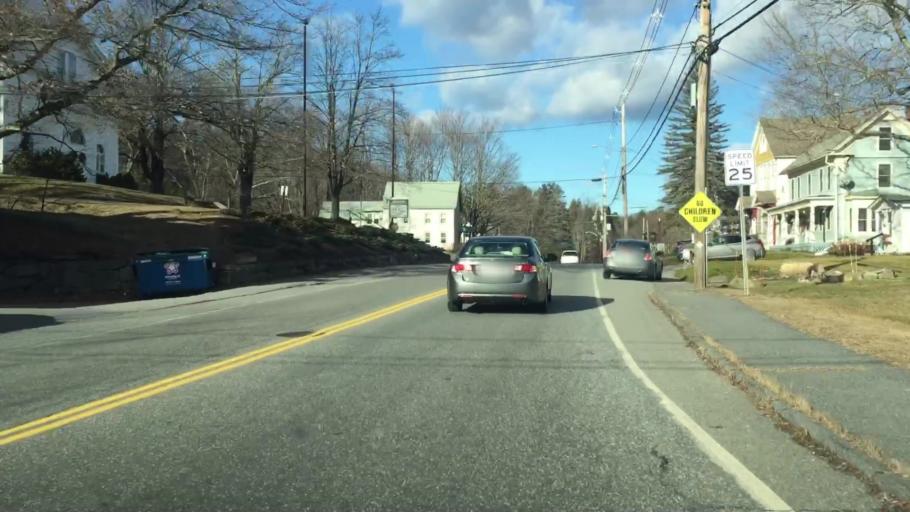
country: US
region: Massachusetts
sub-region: Worcester County
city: West Boylston
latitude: 42.3890
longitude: -71.7934
